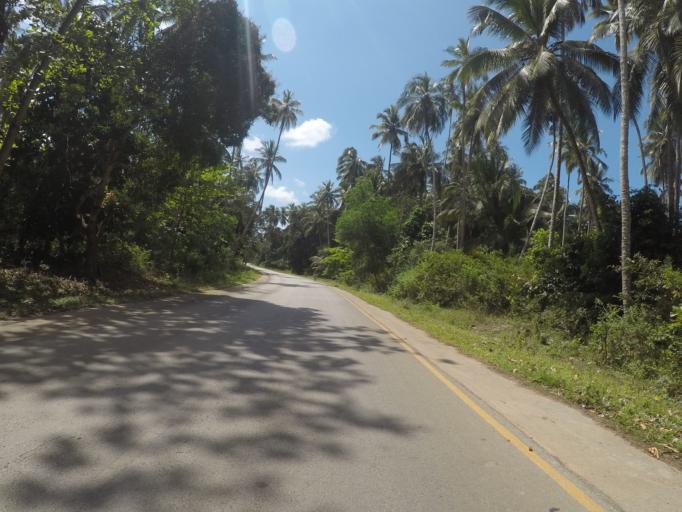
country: TZ
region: Zanzibar Central/South
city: Koani
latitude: -6.1478
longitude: 39.3292
